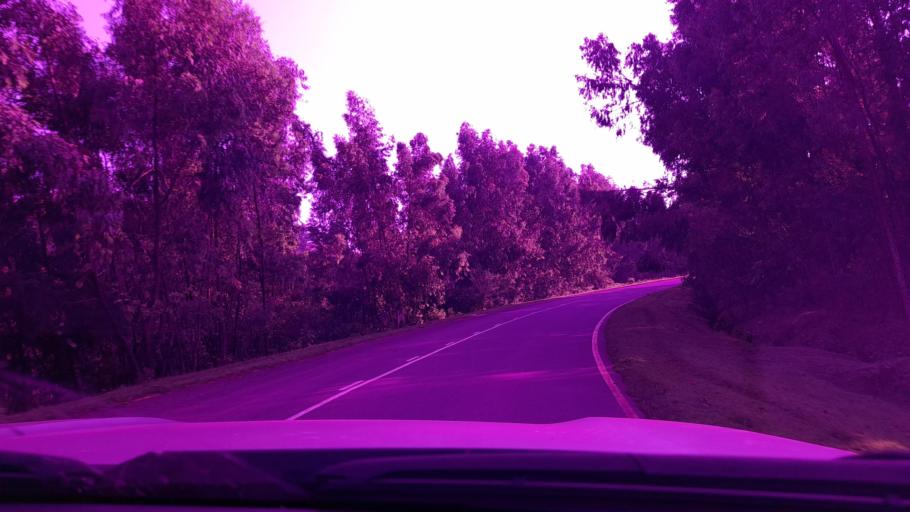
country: ET
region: Oromiya
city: Bedele
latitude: 8.1459
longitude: 36.4582
